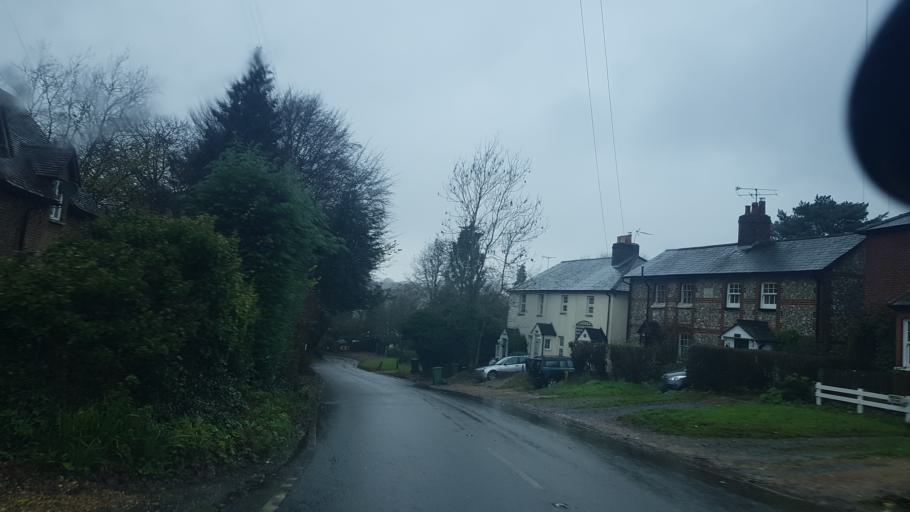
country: GB
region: England
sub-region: Surrey
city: Headley
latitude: 51.2753
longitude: -0.2765
